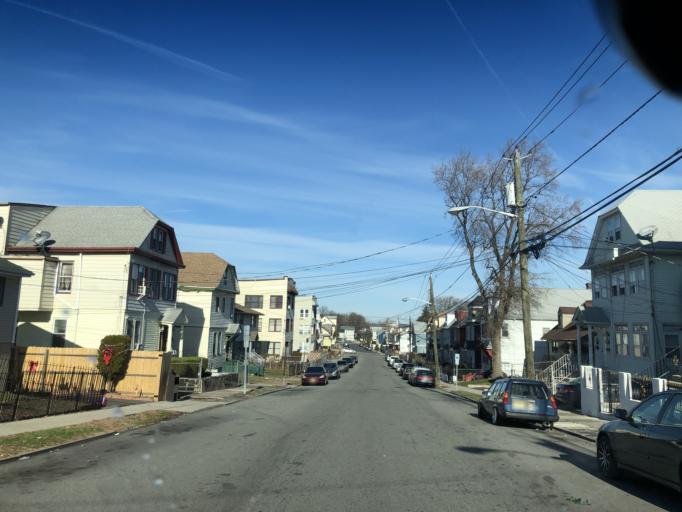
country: US
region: New Jersey
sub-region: Bergen County
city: Fair Lawn
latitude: 40.9219
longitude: -74.1450
